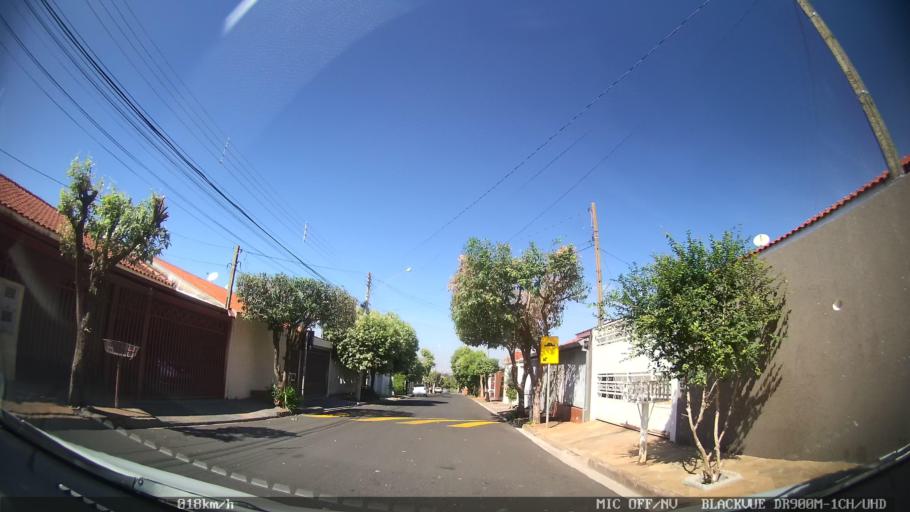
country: BR
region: Sao Paulo
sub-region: Sao Jose Do Rio Preto
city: Sao Jose do Rio Preto
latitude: -20.7676
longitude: -49.3998
